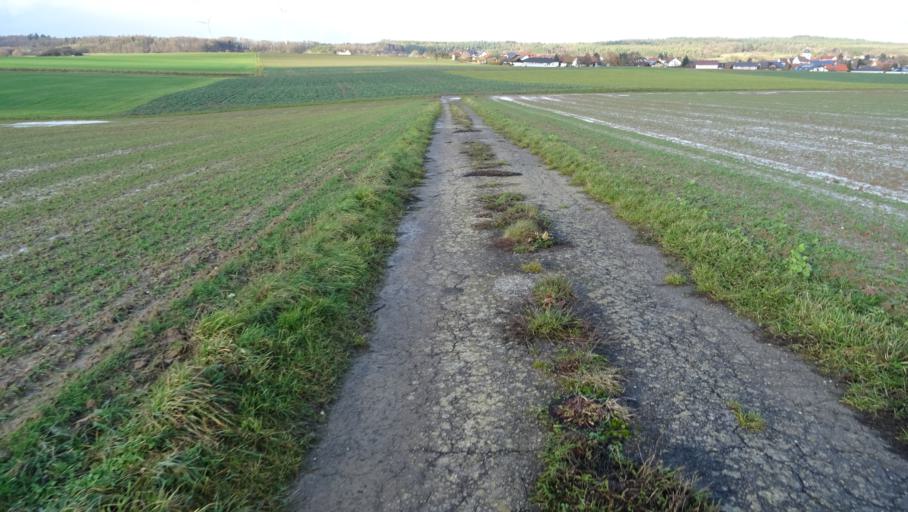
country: DE
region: Baden-Wuerttemberg
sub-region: Karlsruhe Region
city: Seckach
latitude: 49.4362
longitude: 9.2863
